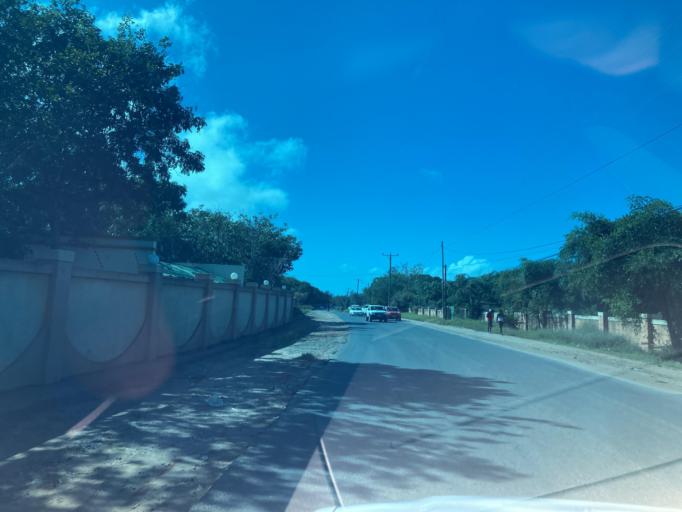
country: MZ
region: Cabo Delgado
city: Pemba
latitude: -12.9658
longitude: 40.5299
